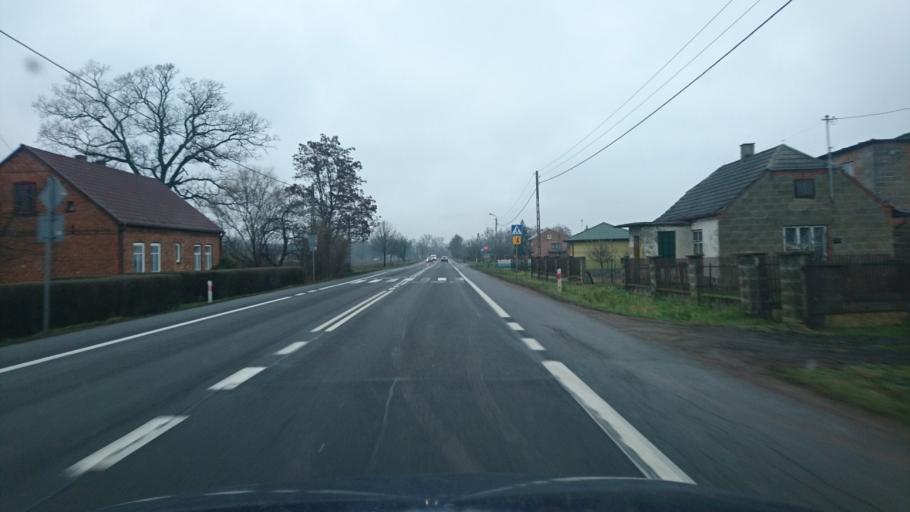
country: PL
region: Lodz Voivodeship
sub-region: Powiat wieruszowski
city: Walichnowy
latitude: 51.2945
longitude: 18.3810
